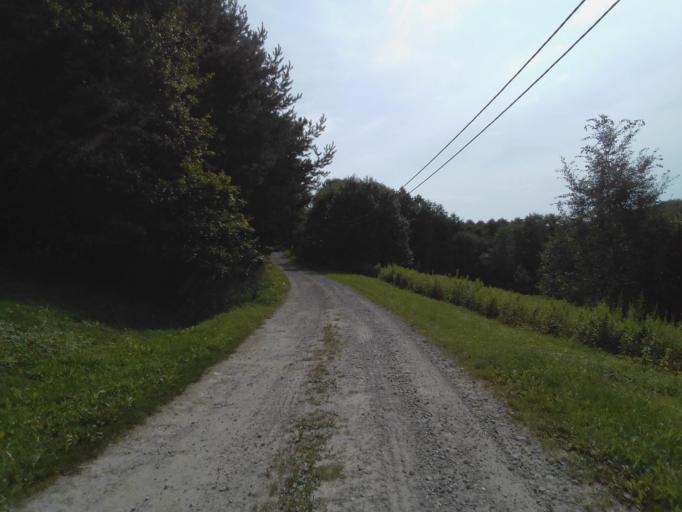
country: PL
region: Subcarpathian Voivodeship
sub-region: Powiat strzyzowski
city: Frysztak
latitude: 49.8671
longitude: 21.5643
